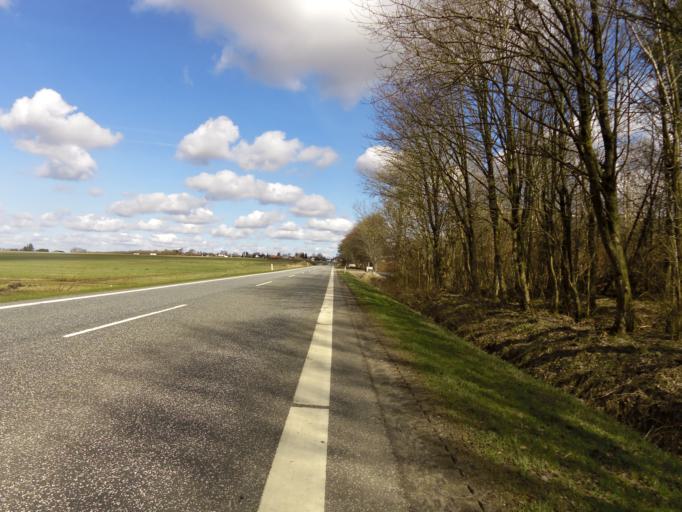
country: DK
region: South Denmark
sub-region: Tonder Kommune
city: Toftlund
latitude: 55.1744
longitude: 9.0572
